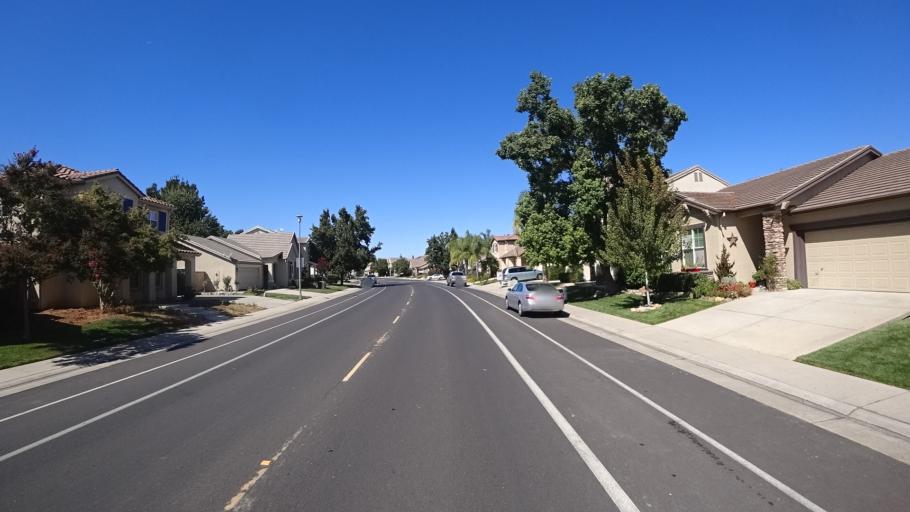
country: US
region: California
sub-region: Sacramento County
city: Elk Grove
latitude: 38.4111
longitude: -121.3460
